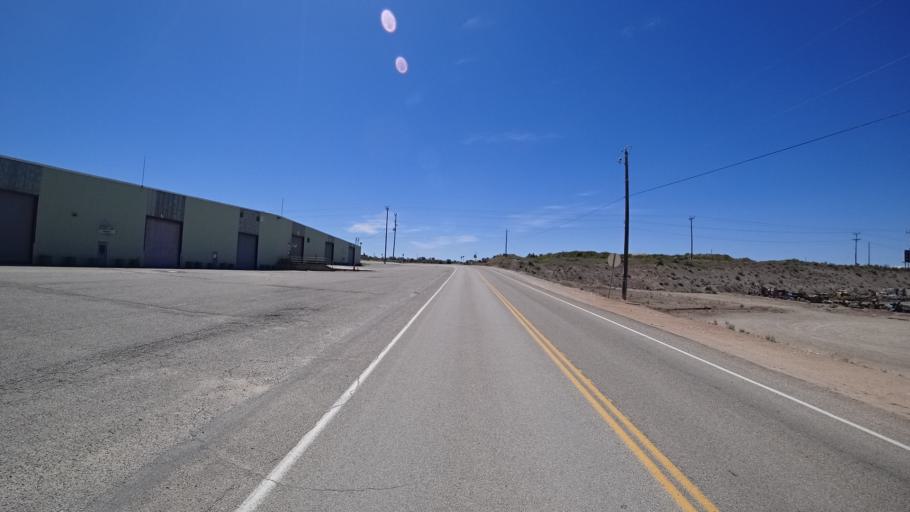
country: US
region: Idaho
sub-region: Ada County
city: Boise
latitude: 43.5617
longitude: -116.1834
